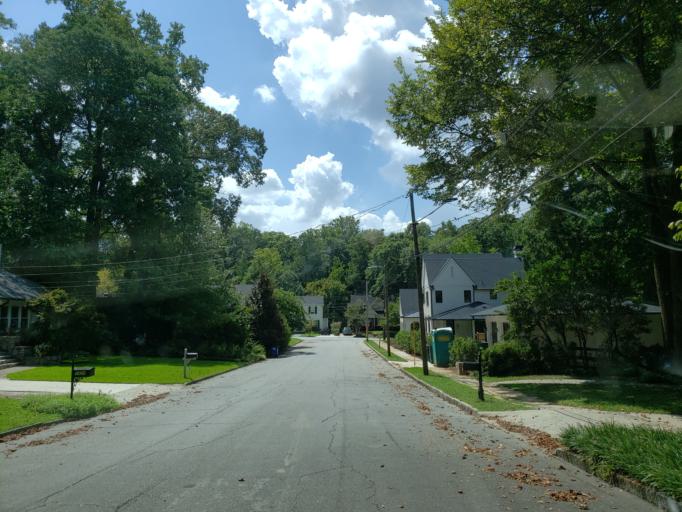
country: US
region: Georgia
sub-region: DeKalb County
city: Druid Hills
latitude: 33.7909
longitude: -84.3594
